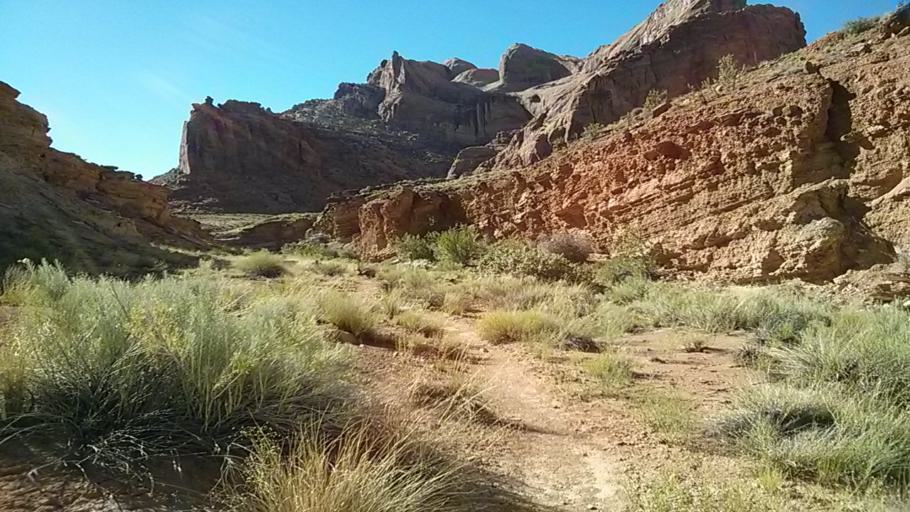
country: US
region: Utah
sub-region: Grand County
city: Moab
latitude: 38.4450
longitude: -109.9556
